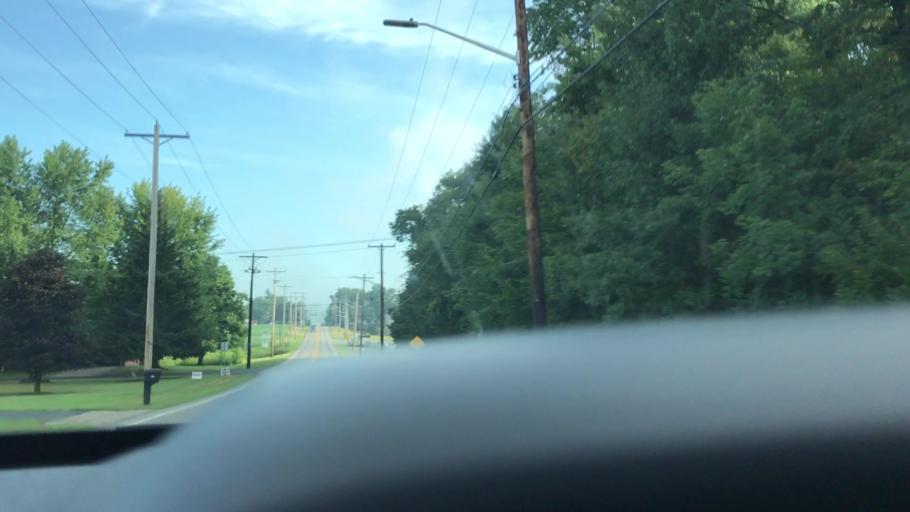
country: US
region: Ohio
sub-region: Stark County
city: Brewster
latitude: 40.7241
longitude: -81.5970
